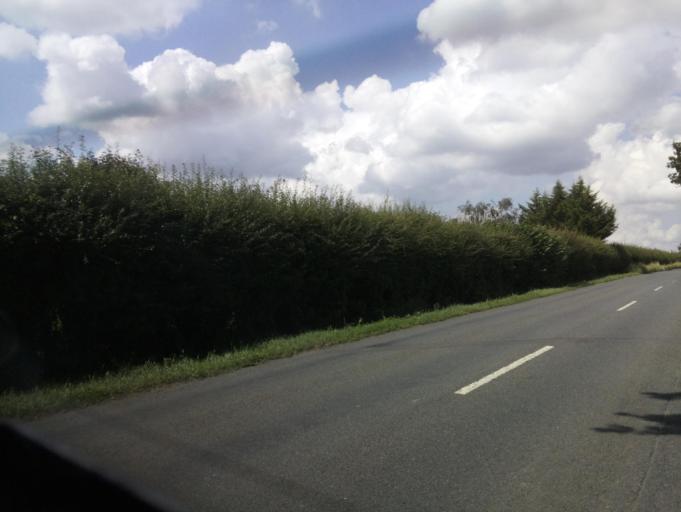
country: GB
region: England
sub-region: Wiltshire
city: Charlton
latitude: 51.5653
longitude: -2.0580
